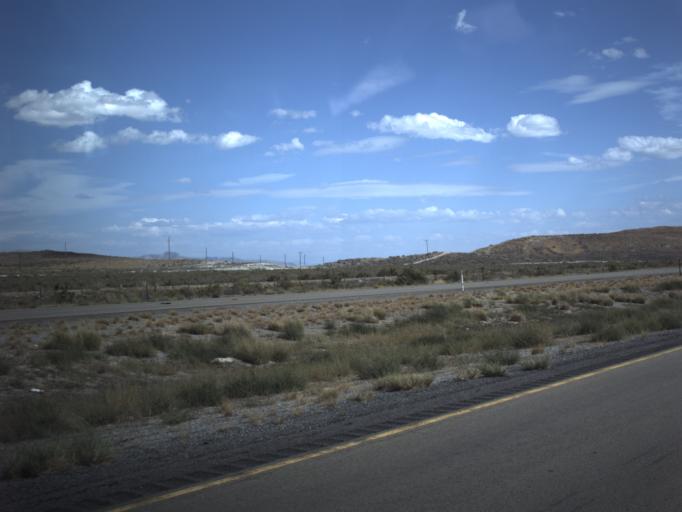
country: US
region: Utah
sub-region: Tooele County
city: Grantsville
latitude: 40.7653
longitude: -112.7864
